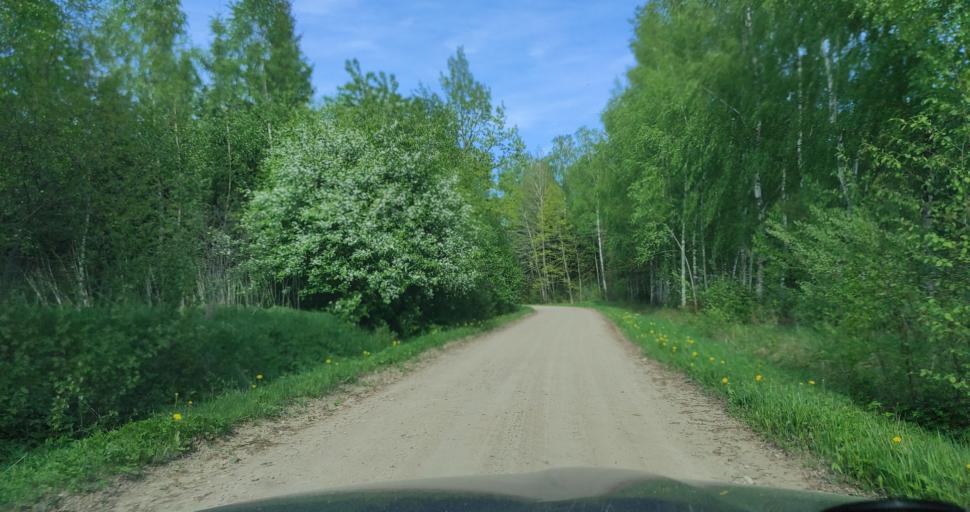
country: LV
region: Kuldigas Rajons
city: Kuldiga
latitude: 56.9331
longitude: 21.8883
